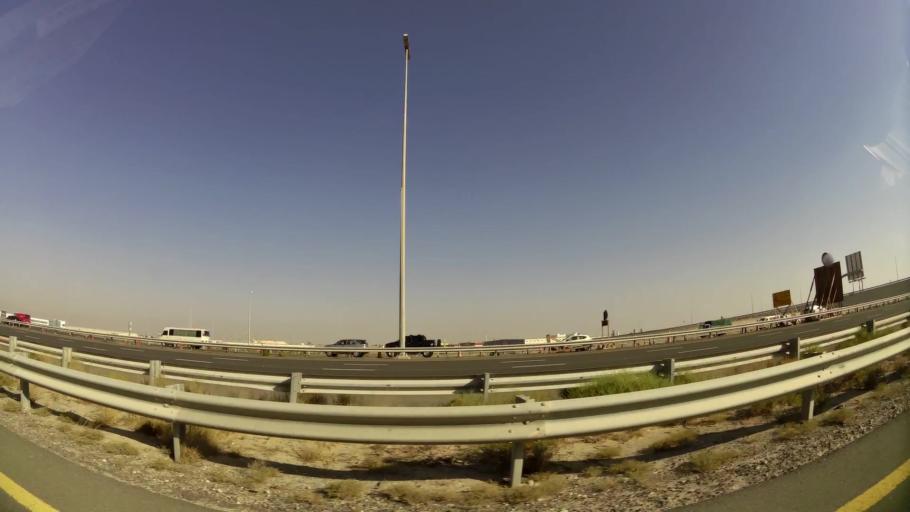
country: AE
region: Dubai
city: Dubai
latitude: 24.9481
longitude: 55.0642
